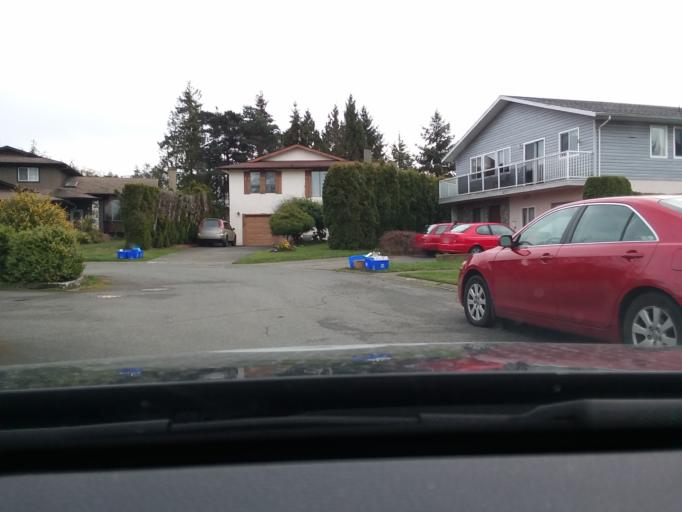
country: CA
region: British Columbia
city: Oak Bay
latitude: 48.4771
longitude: -123.3247
